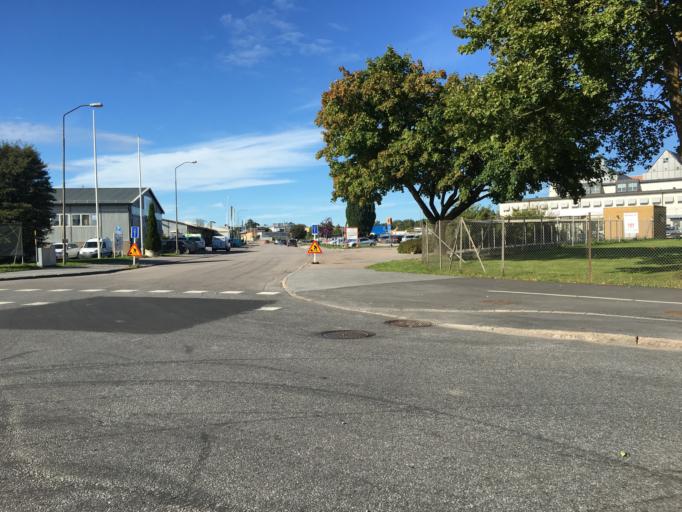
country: SE
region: Uppsala
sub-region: Uppsala Kommun
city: Uppsala
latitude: 59.8494
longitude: 17.6737
